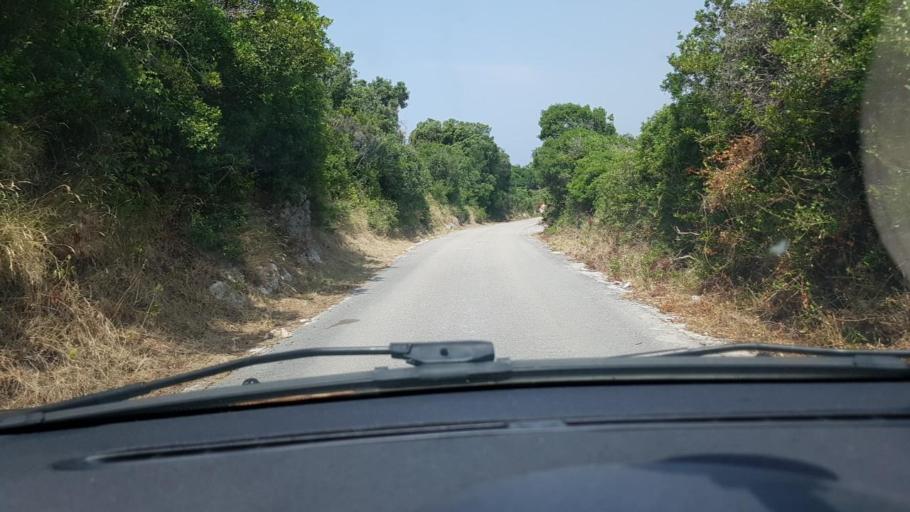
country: ME
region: Herceg Novi
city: Herceg-Novi
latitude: 42.4051
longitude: 18.5127
